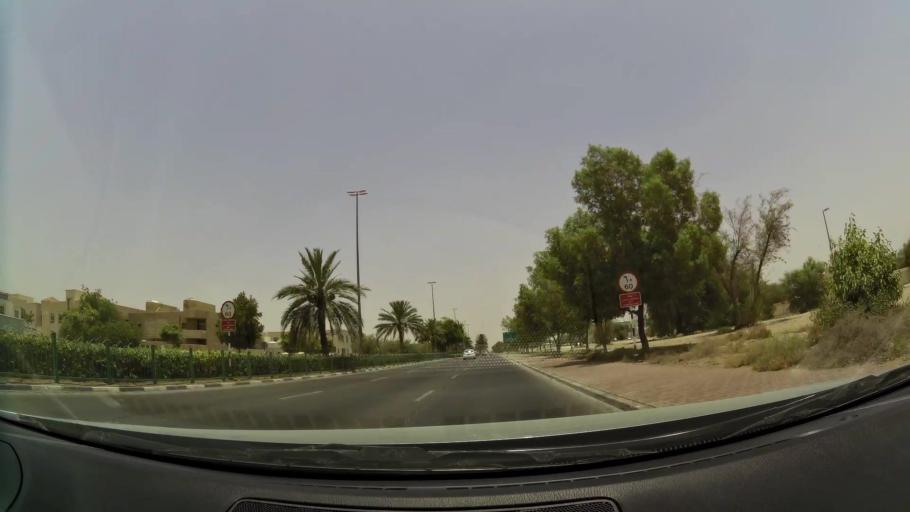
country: AE
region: Abu Dhabi
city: Al Ain
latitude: 24.2103
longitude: 55.7465
